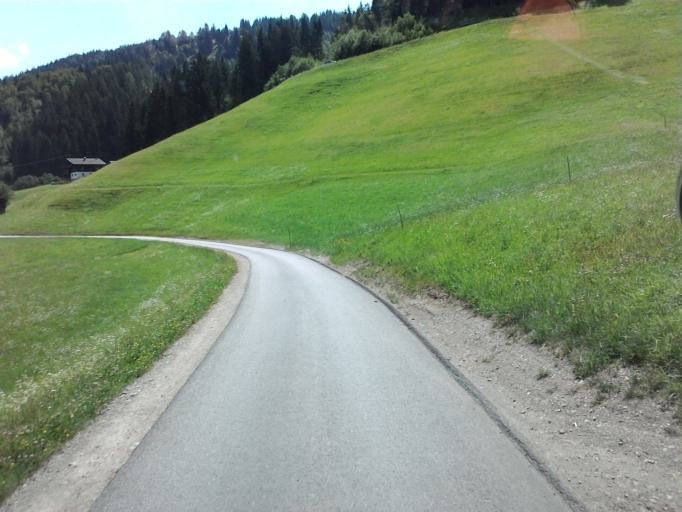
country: AT
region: Tyrol
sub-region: Politischer Bezirk Lienz
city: Untertilliach
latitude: 46.6996
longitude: 12.7467
